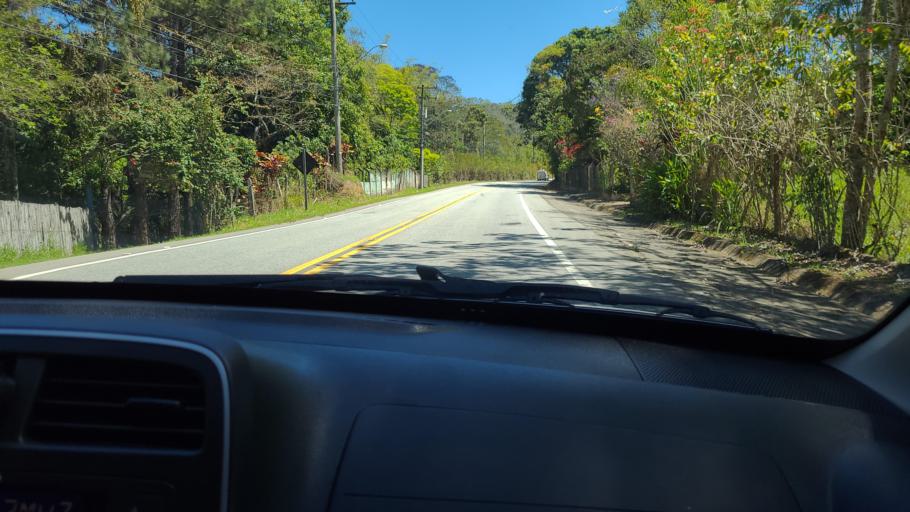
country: BR
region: Sao Paulo
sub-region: Tremembe
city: Tremembe
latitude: -22.8795
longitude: -45.5749
